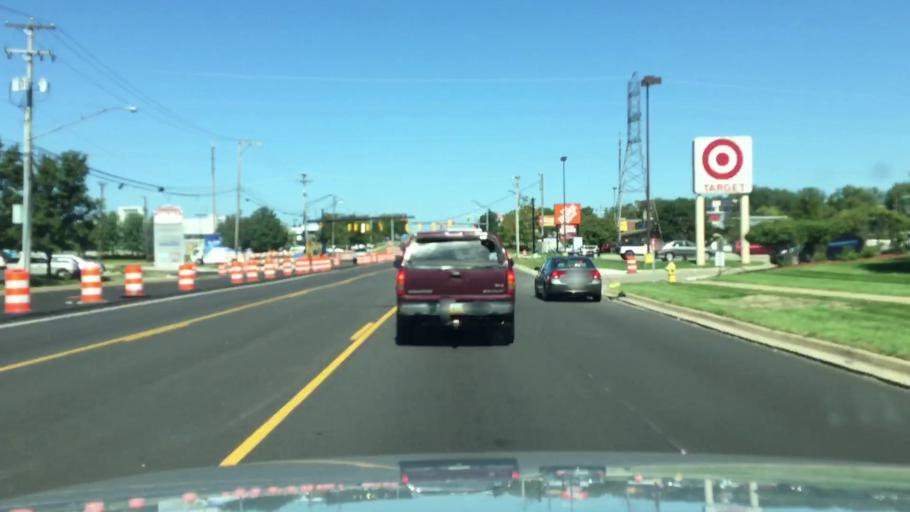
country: US
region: Michigan
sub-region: Kalamazoo County
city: Portage
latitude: 42.2180
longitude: -85.5894
